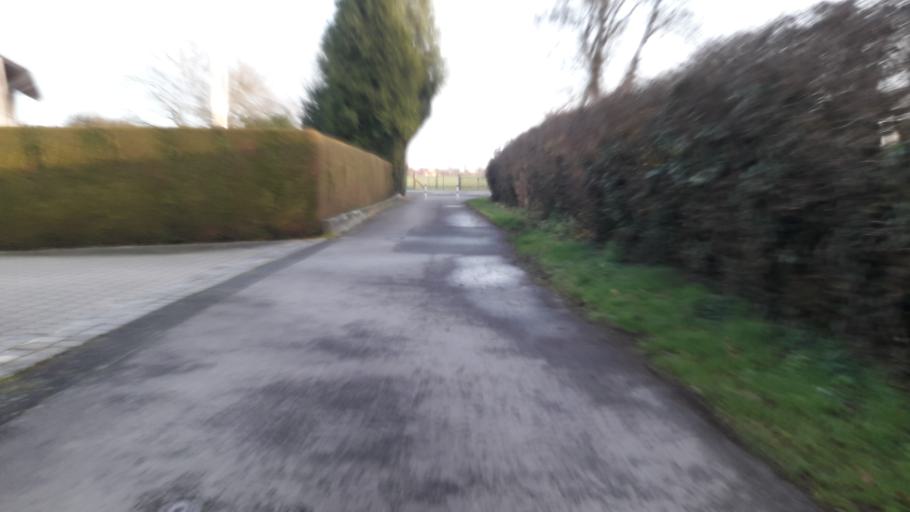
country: DE
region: North Rhine-Westphalia
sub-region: Regierungsbezirk Arnsberg
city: Soest
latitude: 51.5663
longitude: 8.0595
